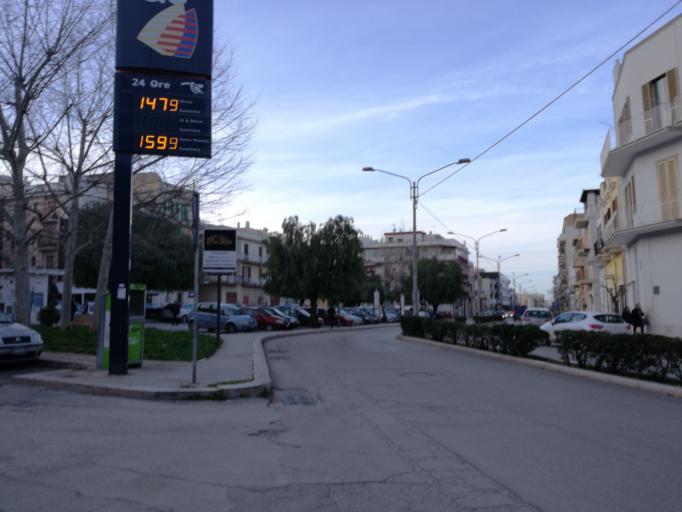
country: IT
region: Apulia
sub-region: Provincia di Bari
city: Corato
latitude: 41.1514
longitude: 16.4075
